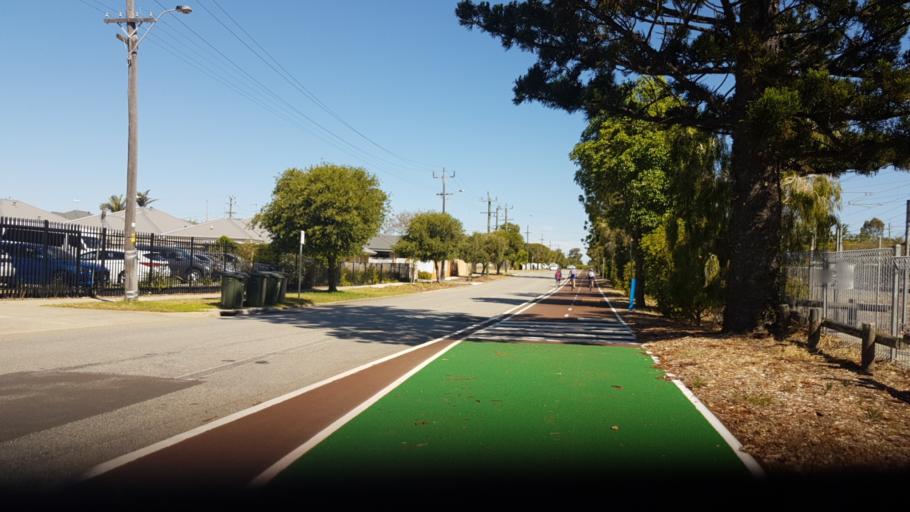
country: AU
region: Western Australia
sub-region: Victoria Park
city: Victoria Park
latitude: -31.9815
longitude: 115.9120
